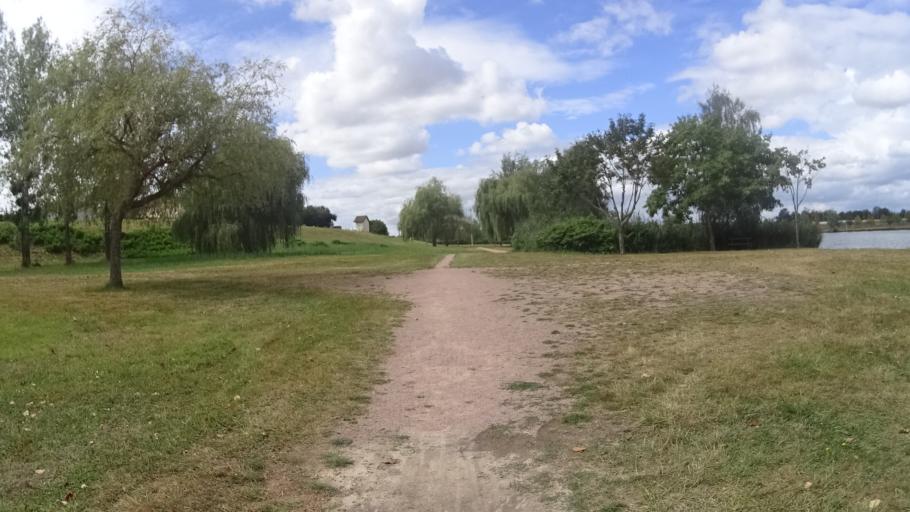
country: FR
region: Bourgogne
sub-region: Departement de Saone-et-Loire
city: Saint-Leu
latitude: 46.7371
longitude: 4.4881
